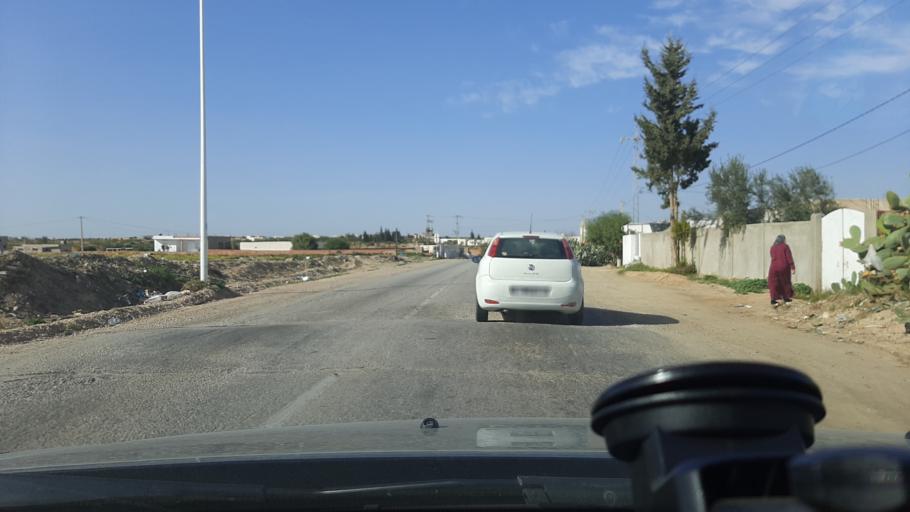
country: TN
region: Safaqis
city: Sfax
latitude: 34.8310
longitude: 10.5970
